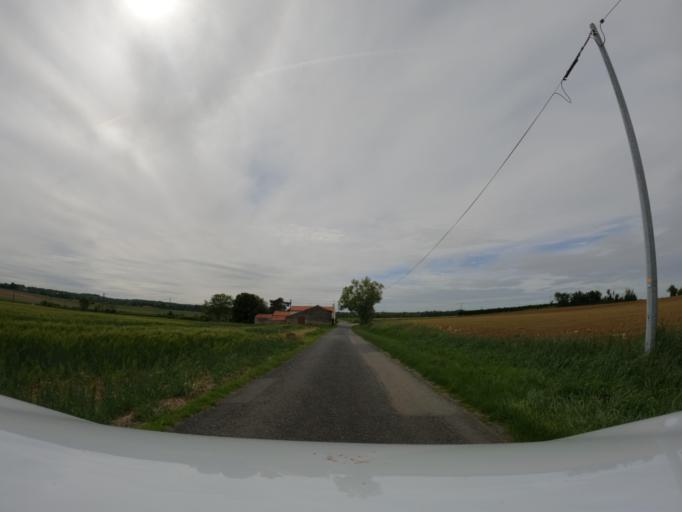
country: FR
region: Pays de la Loire
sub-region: Departement de la Vendee
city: Saint-Hilaire-des-Loges
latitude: 46.5038
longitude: -0.6473
